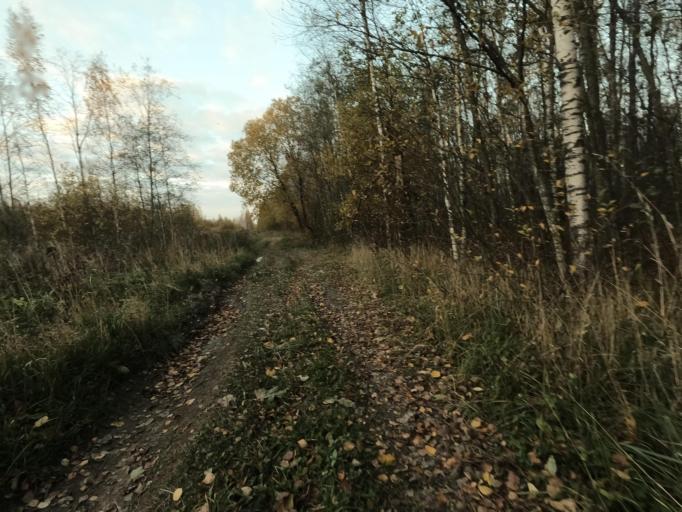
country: RU
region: Leningrad
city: Mga
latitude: 59.8174
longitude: 31.1779
